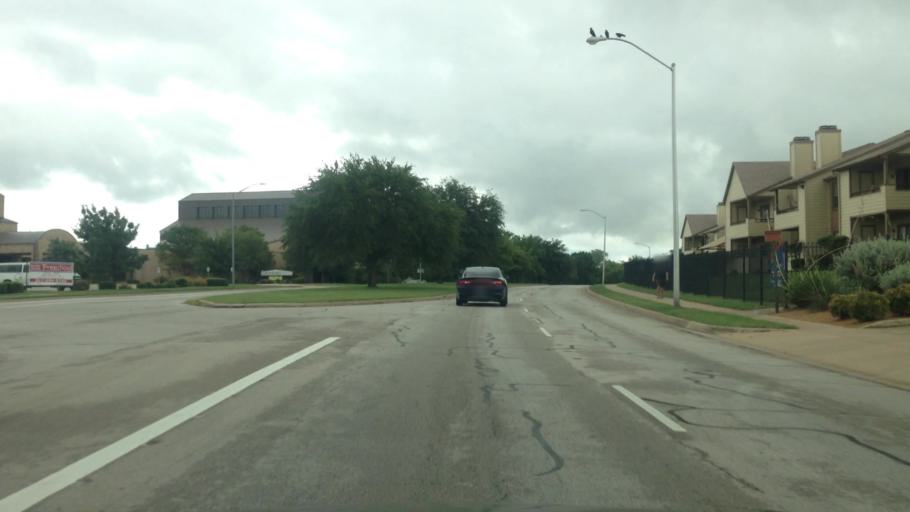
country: US
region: Texas
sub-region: Tarrant County
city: Edgecliff Village
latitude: 32.6328
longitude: -97.3893
